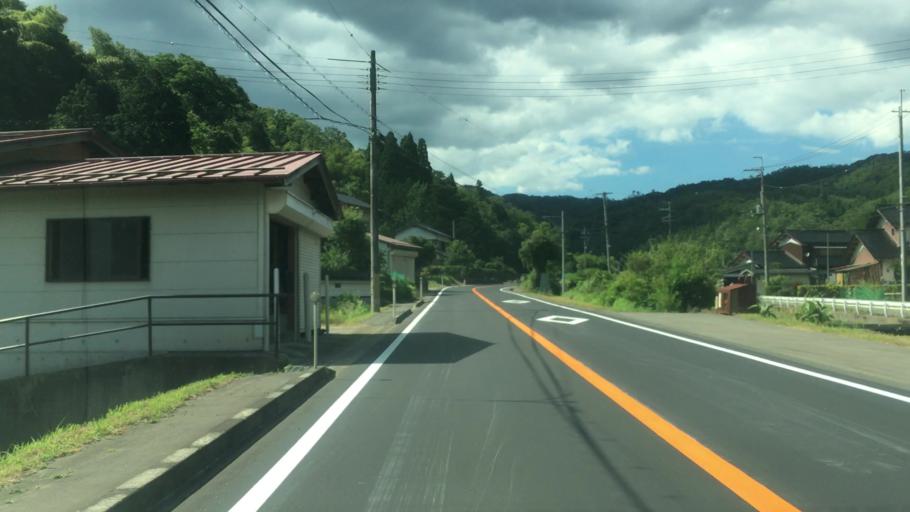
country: JP
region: Hyogo
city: Toyooka
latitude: 35.5005
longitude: 134.7778
